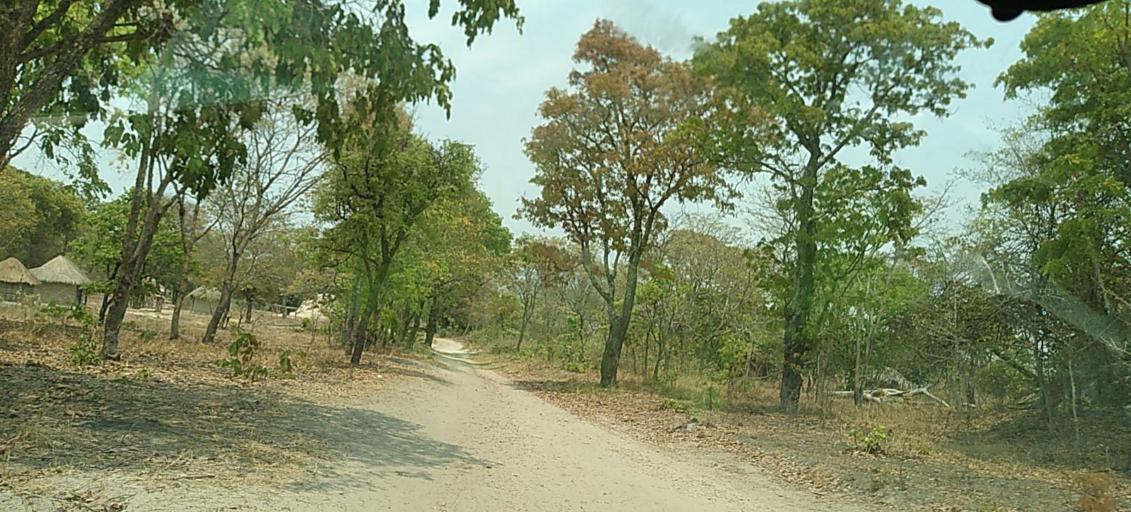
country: ZM
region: North-Western
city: Kabompo
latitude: -13.5396
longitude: 24.4529
